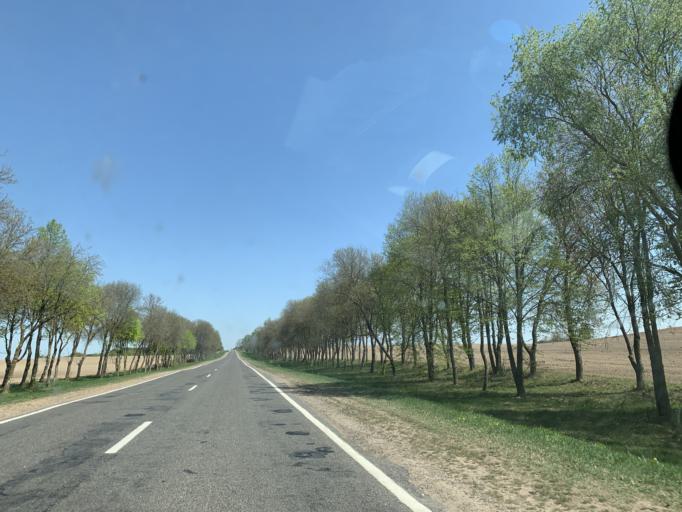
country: BY
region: Minsk
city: Nyasvizh
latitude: 53.2300
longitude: 26.7828
